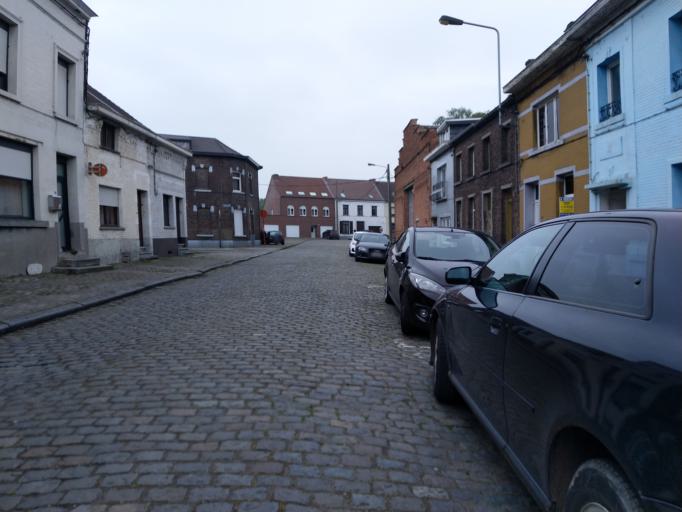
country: BE
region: Wallonia
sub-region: Province du Hainaut
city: Quaregnon
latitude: 50.4518
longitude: 3.8807
